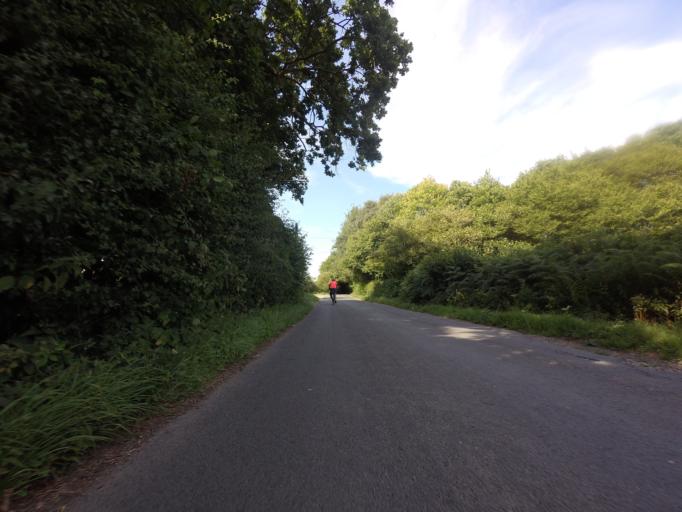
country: GB
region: England
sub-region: East Sussex
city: Rye
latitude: 50.9891
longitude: 0.6763
